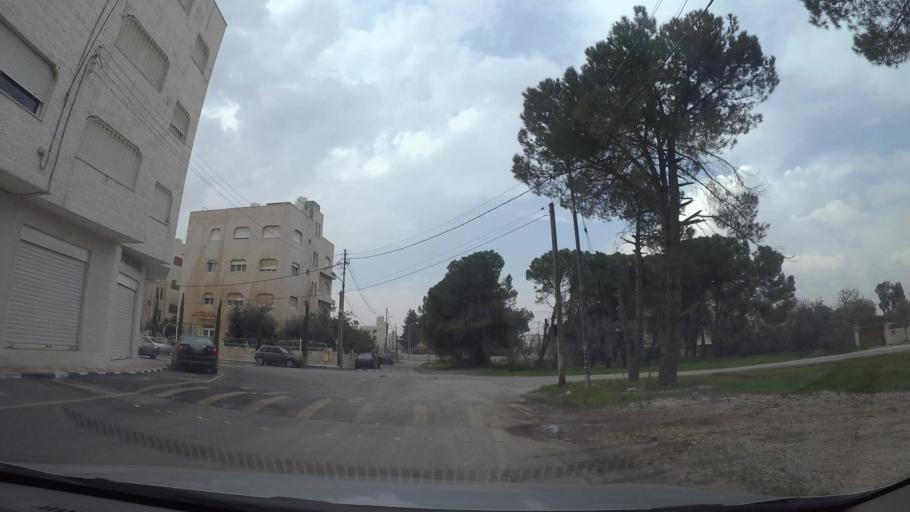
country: JO
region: Amman
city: Umm as Summaq
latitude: 31.8906
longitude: 35.8505
